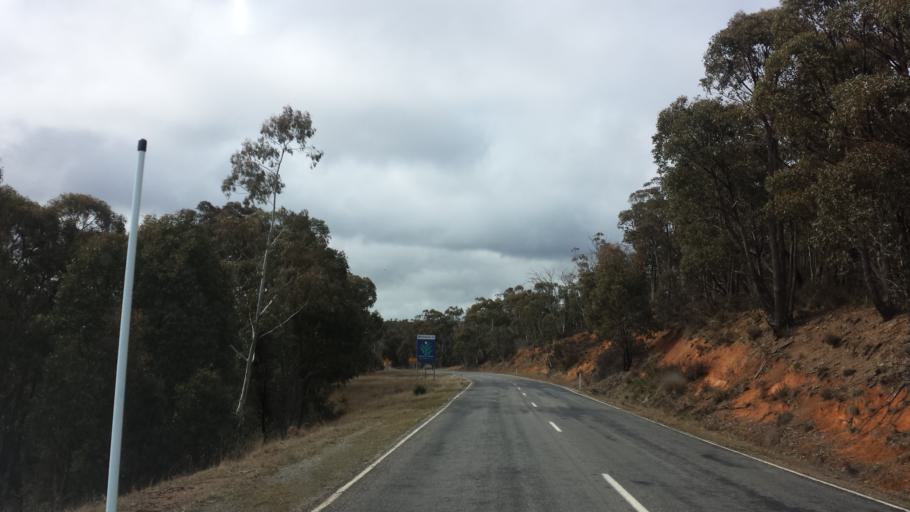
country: AU
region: Victoria
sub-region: Alpine
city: Mount Beauty
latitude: -37.0821
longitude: 147.3798
